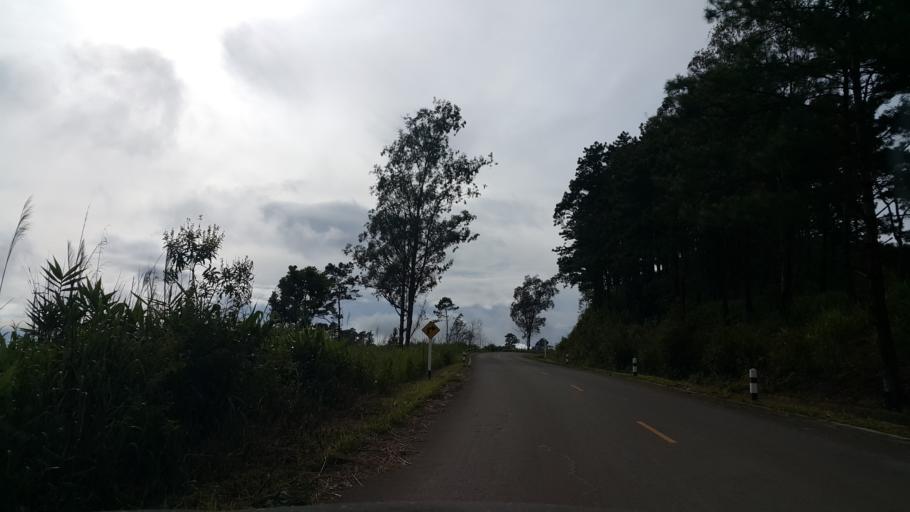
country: TH
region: Chiang Mai
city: Chaem Luang
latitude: 18.9517
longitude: 98.4439
